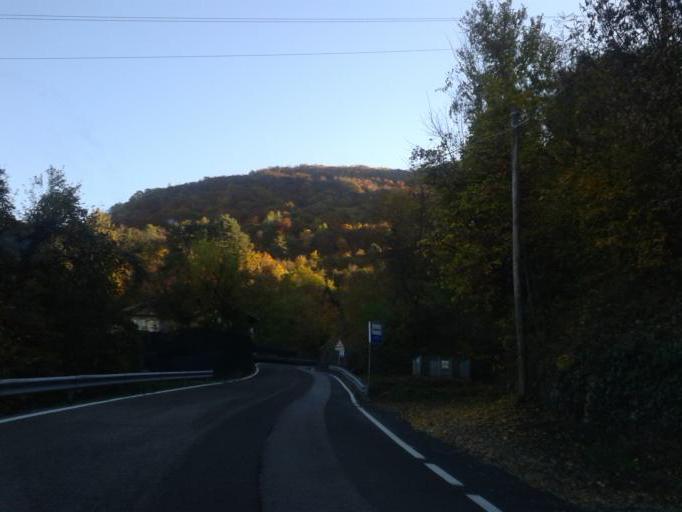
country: IT
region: Trentino-Alto Adige
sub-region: Provincia di Trento
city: Trento
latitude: 46.0724
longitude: 11.0992
